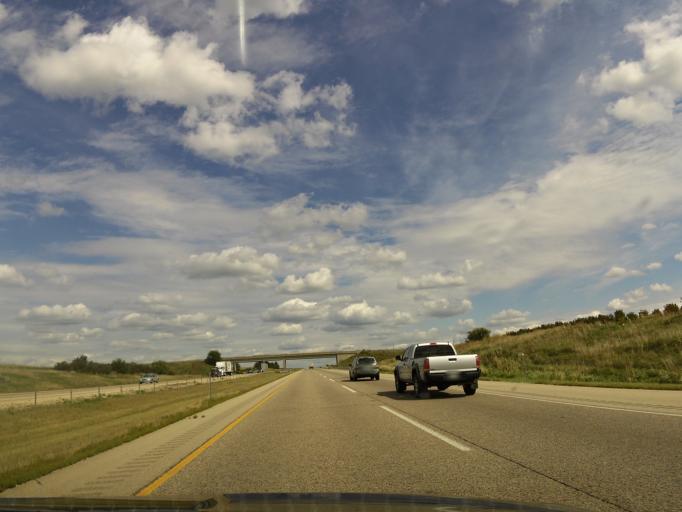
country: US
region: Illinois
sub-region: Ogle County
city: Rochelle
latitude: 41.9053
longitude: -88.9831
